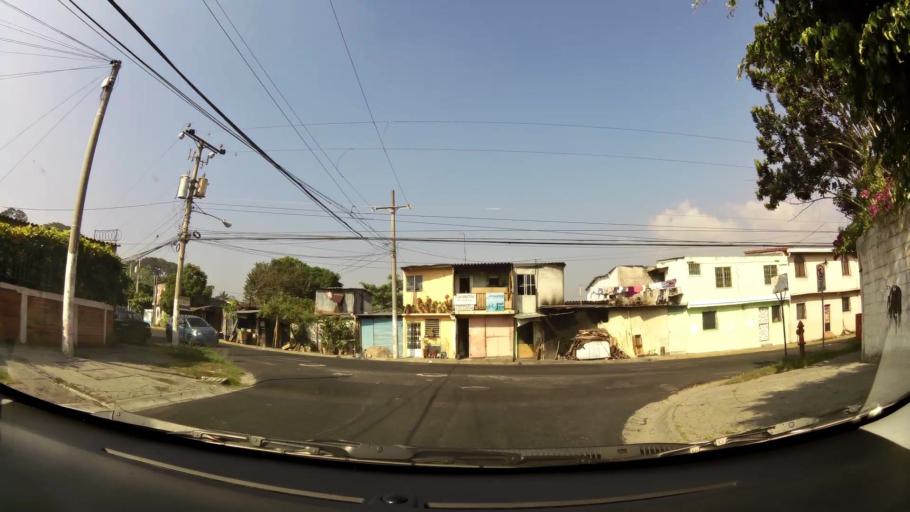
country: SV
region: La Libertad
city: Antiguo Cuscatlan
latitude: 13.6751
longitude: -89.2356
